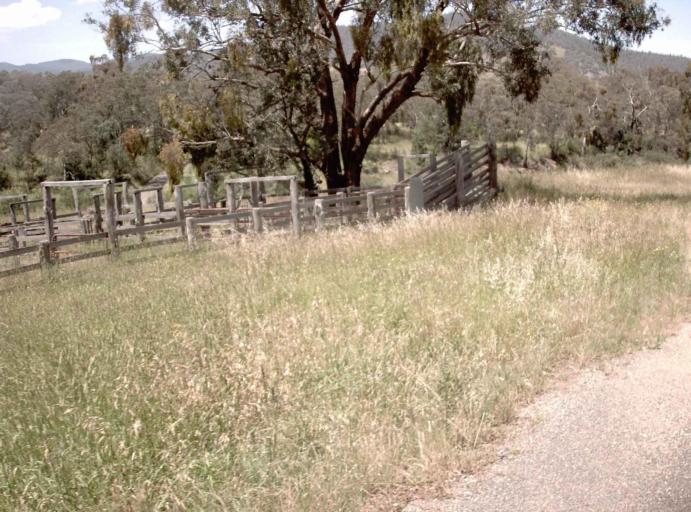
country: AU
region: Victoria
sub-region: East Gippsland
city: Bairnsdale
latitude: -37.4077
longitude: 147.8361
